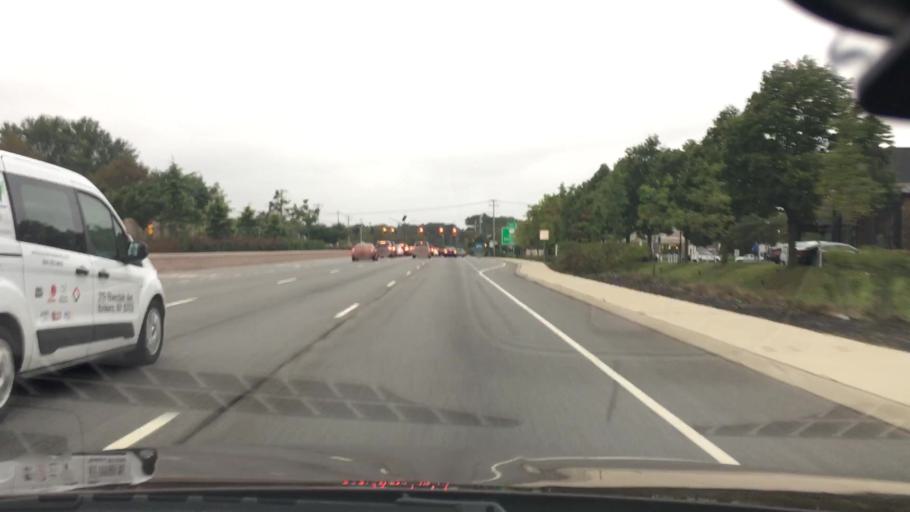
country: US
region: New York
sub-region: Suffolk County
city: Village of the Branch
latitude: 40.8380
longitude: -73.1830
